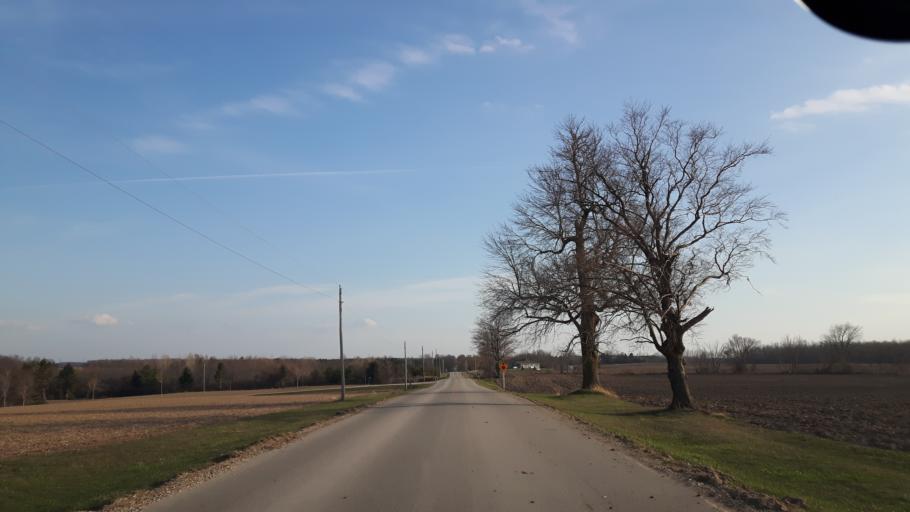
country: CA
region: Ontario
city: Goderich
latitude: 43.6888
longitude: -81.6645
